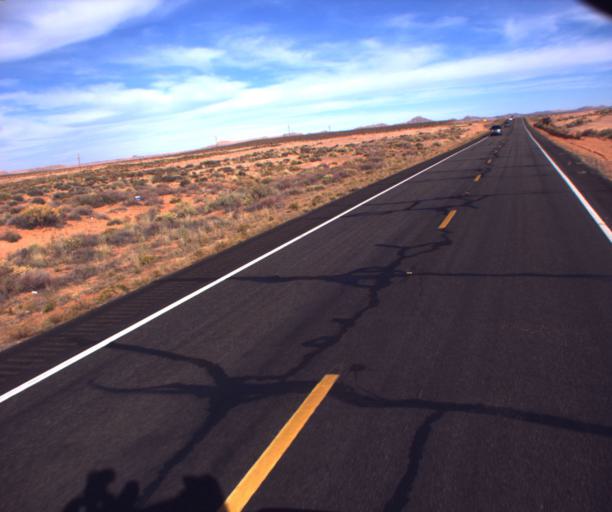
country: US
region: Arizona
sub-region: Apache County
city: Many Farms
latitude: 36.9396
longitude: -109.6820
